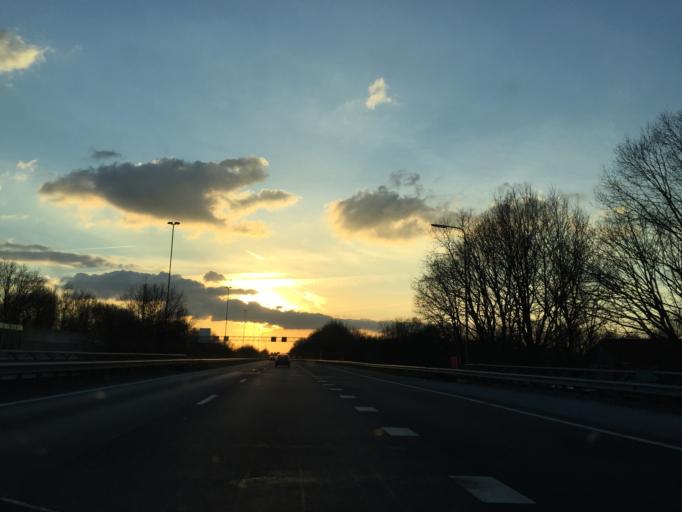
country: NL
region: North Brabant
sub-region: Gemeente Dongen
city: Dongen
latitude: 51.5520
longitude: 4.9462
